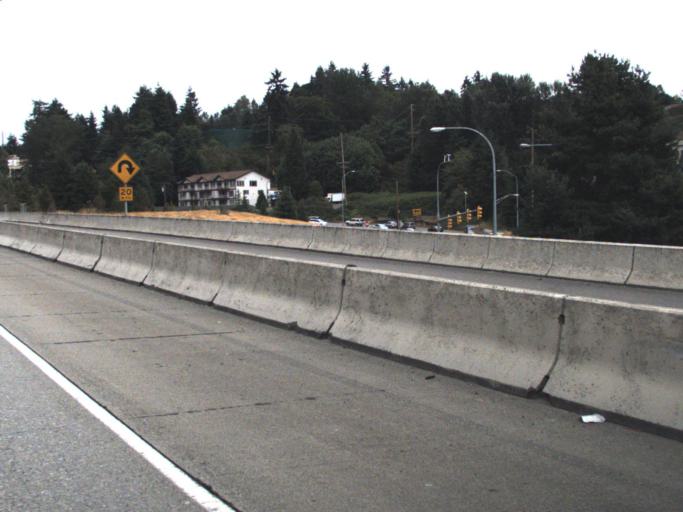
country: US
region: Washington
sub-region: King County
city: Renton
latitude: 47.4834
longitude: -122.1969
